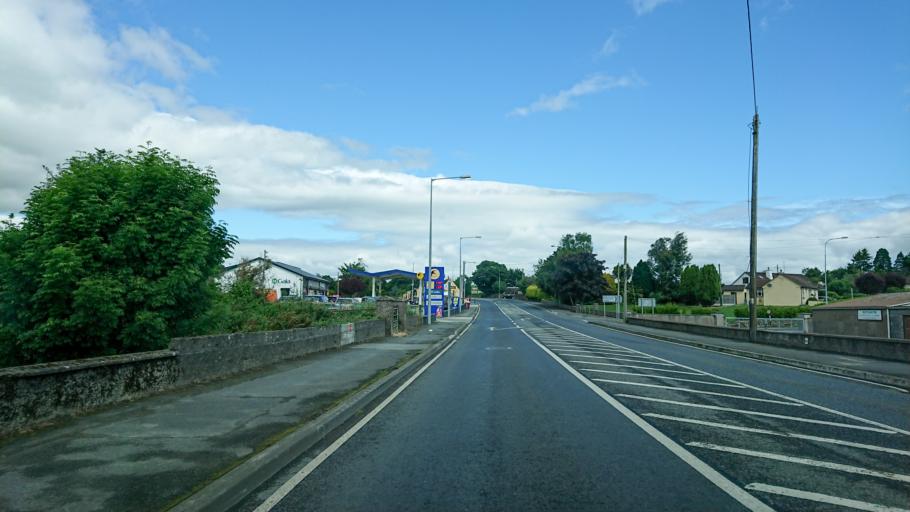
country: IE
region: Leinster
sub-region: Kilkenny
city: Mooncoin
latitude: 52.2336
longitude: -7.2432
